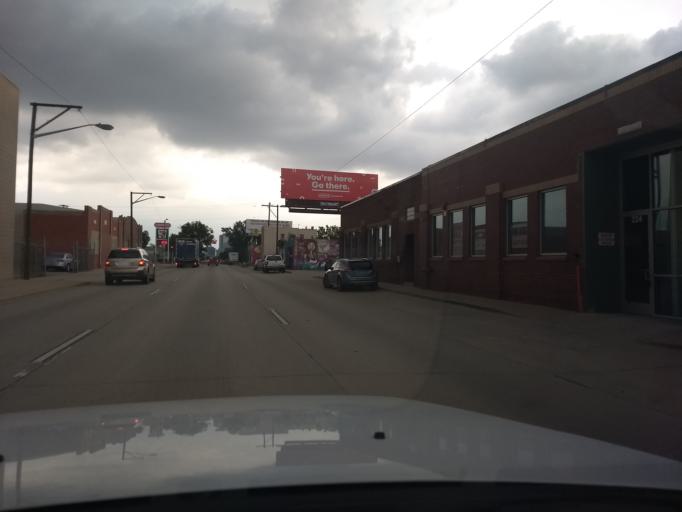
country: US
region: Colorado
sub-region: Denver County
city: Denver
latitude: 39.7199
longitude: -104.9986
